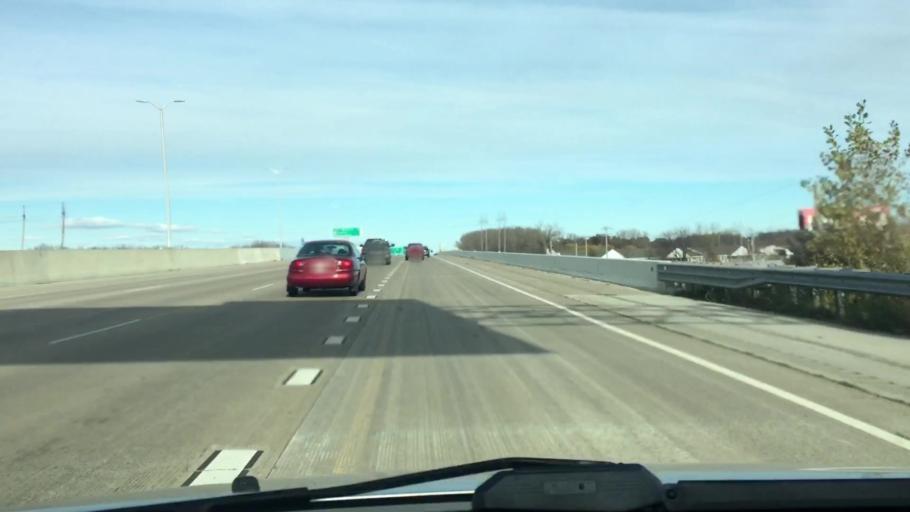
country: US
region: Wisconsin
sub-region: Brown County
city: Howard
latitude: 44.5466
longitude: -88.0699
